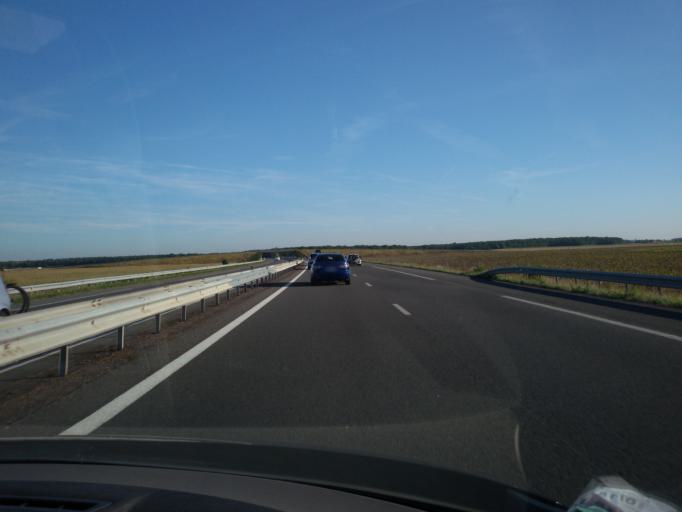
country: FR
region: Centre
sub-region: Departement du Cher
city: Levet
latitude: 46.8585
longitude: 2.4283
